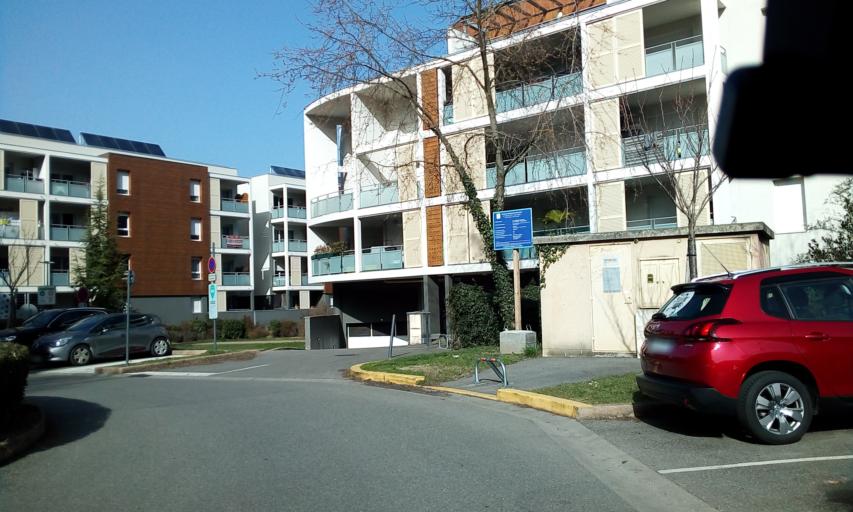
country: FR
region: Rhone-Alpes
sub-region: Departement de l'Isere
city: Gieres
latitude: 45.1830
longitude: 5.7840
